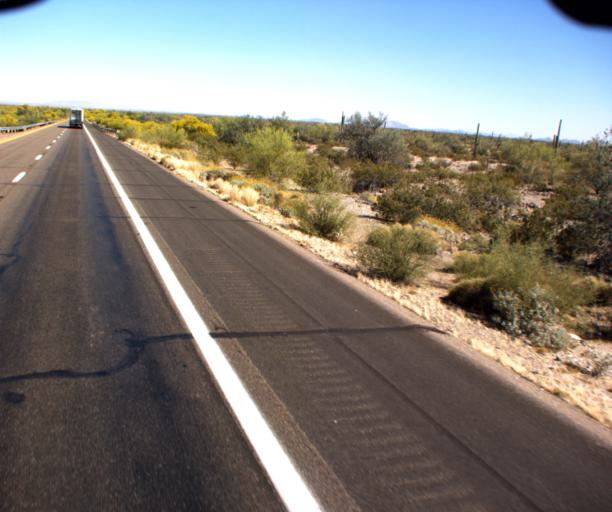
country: US
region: Arizona
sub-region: Pinal County
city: Maricopa
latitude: 32.8309
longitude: -112.0473
